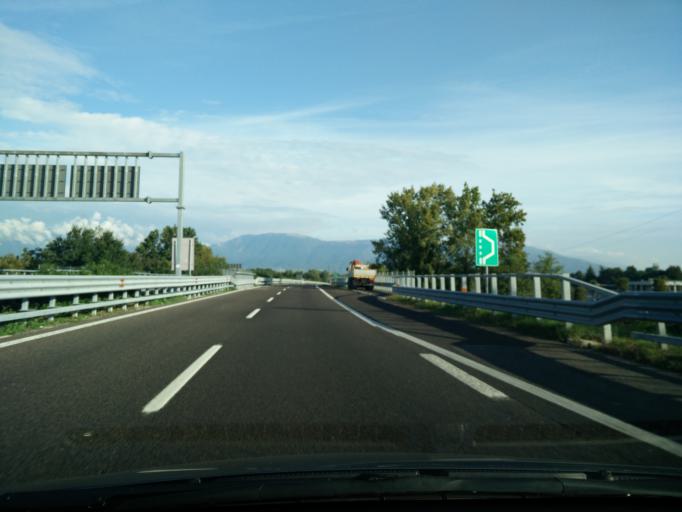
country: IT
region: Veneto
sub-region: Provincia di Treviso
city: San Vendemiano
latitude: 45.8867
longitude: 12.3409
